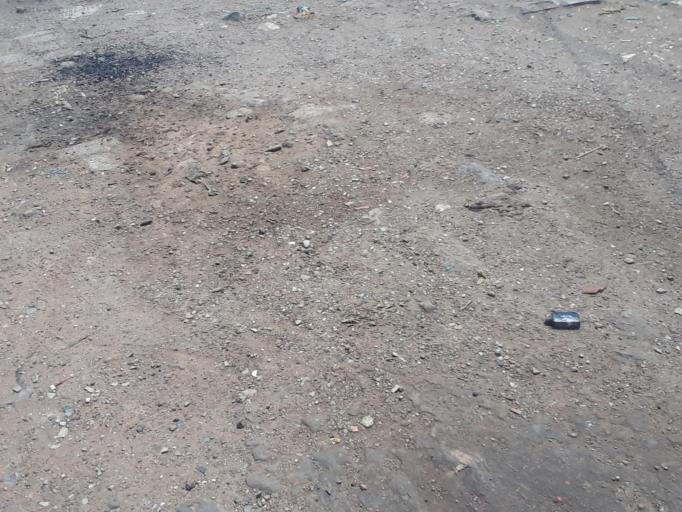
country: ZM
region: Lusaka
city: Lusaka
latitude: -15.3646
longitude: 28.2924
